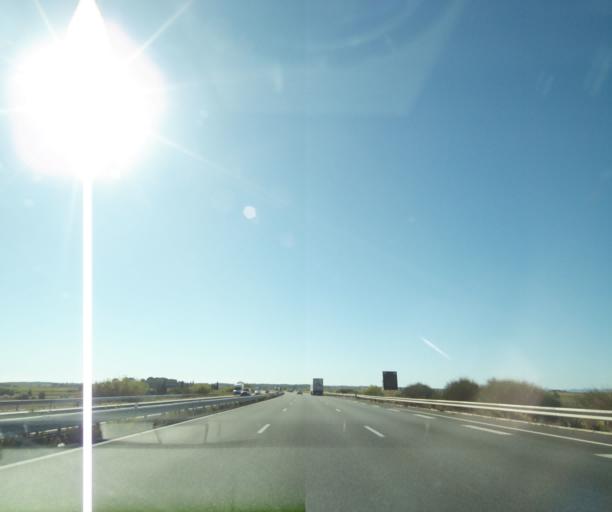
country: FR
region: Languedoc-Roussillon
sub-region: Departement de l'Herault
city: Bessan
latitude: 43.3754
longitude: 3.4080
